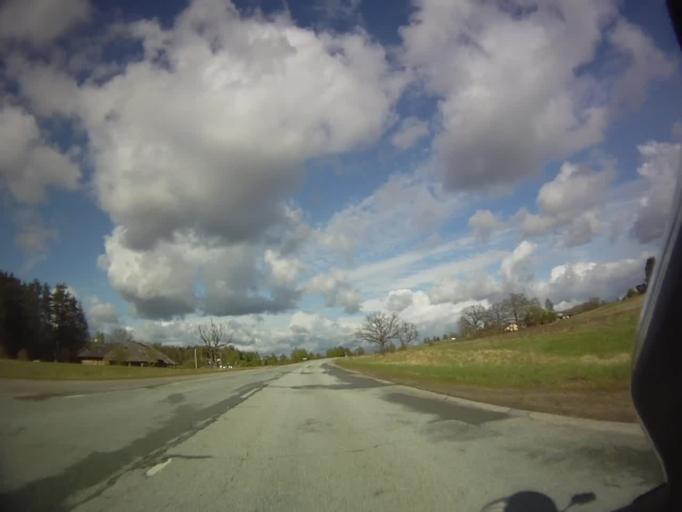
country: LV
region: Sigulda
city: Sigulda
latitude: 57.1833
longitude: 24.8307
